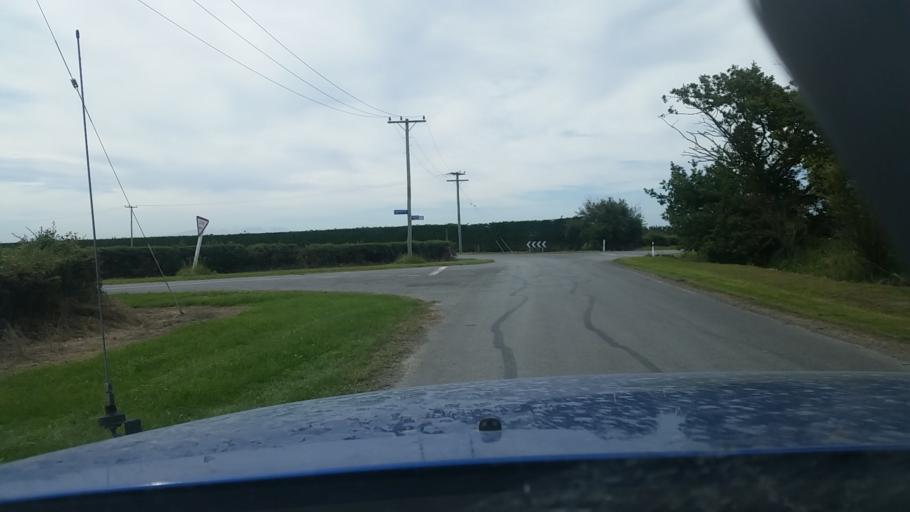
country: NZ
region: Canterbury
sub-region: Ashburton District
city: Tinwald
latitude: -44.0362
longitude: 171.7831
